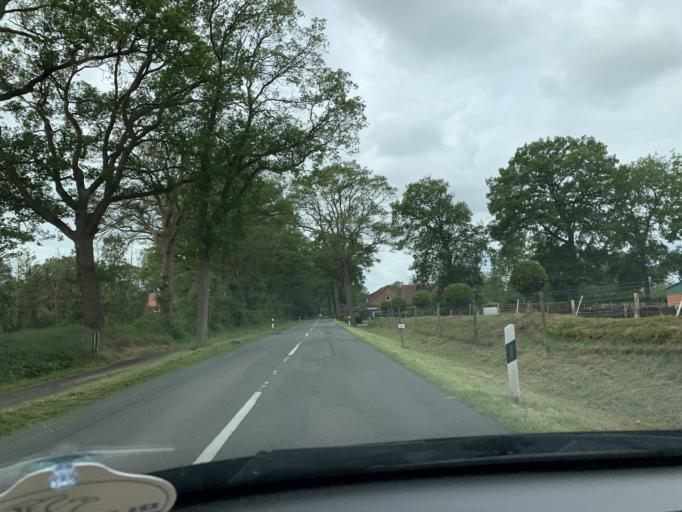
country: DE
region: Lower Saxony
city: Bockhorn
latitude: 53.3541
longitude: 8.0601
